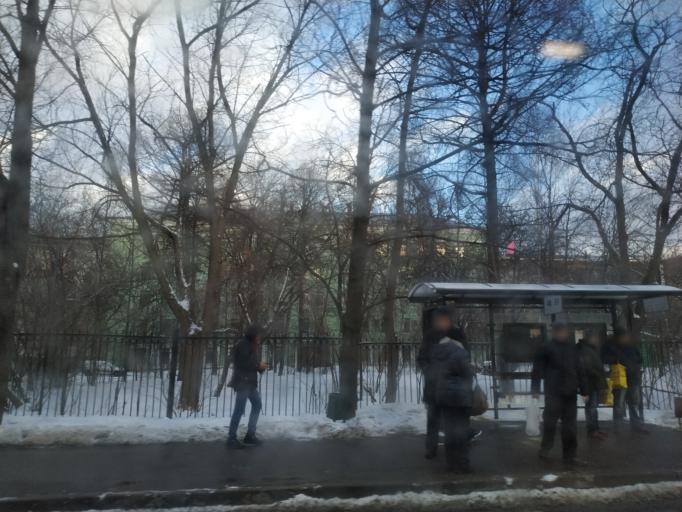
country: RU
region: Moskovskaya
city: Izmaylovo
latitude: 55.7924
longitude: 37.8194
